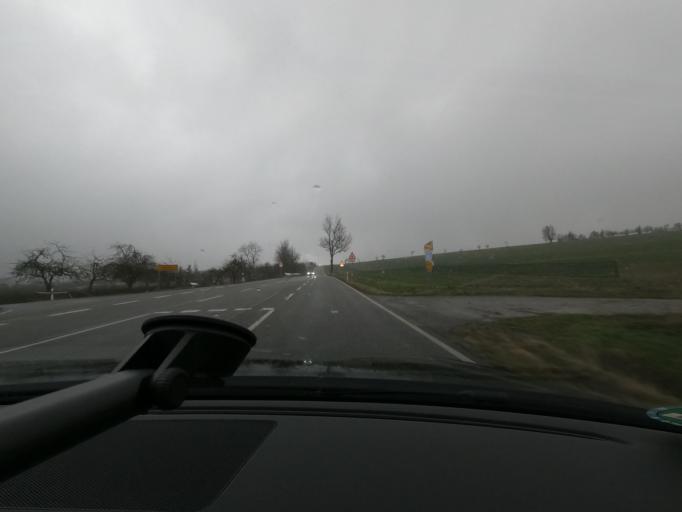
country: DE
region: Thuringia
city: Helmsdorf
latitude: 51.2947
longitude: 10.3431
